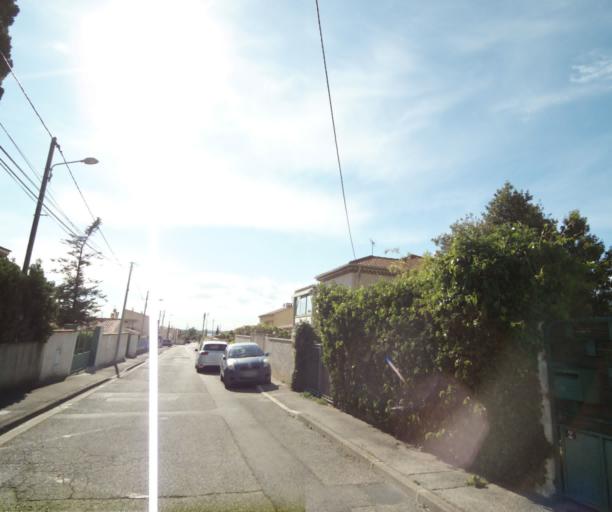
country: FR
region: Provence-Alpes-Cote d'Azur
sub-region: Departement des Bouches-du-Rhone
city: Rognac
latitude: 43.4856
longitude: 5.2300
